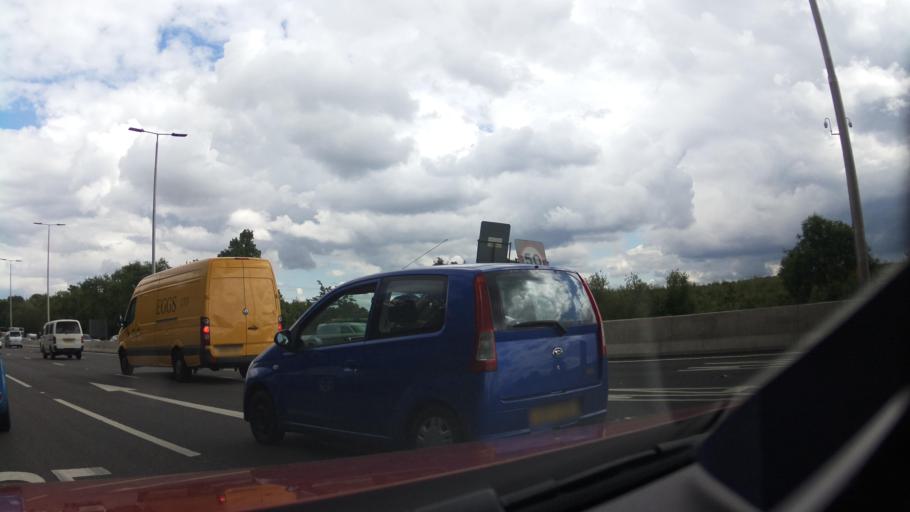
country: GB
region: England
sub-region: Surrey
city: Colnbrook
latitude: 51.4938
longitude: -0.5238
